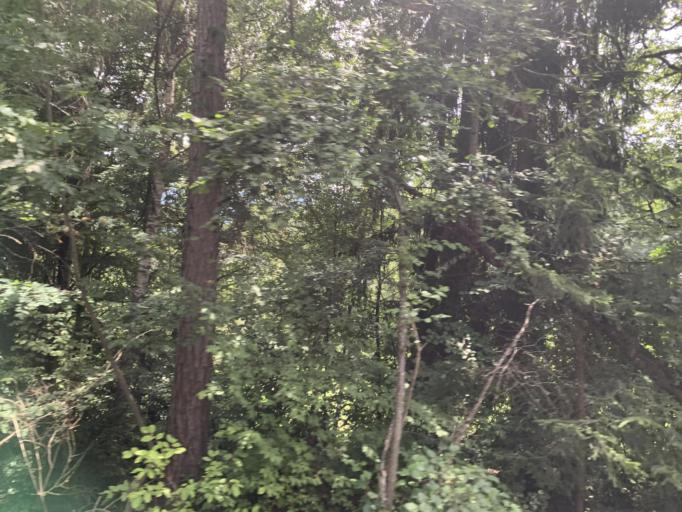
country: IT
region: Trentino-Alto Adige
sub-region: Bolzano
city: Renon - Ritten
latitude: 46.5346
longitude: 11.4411
